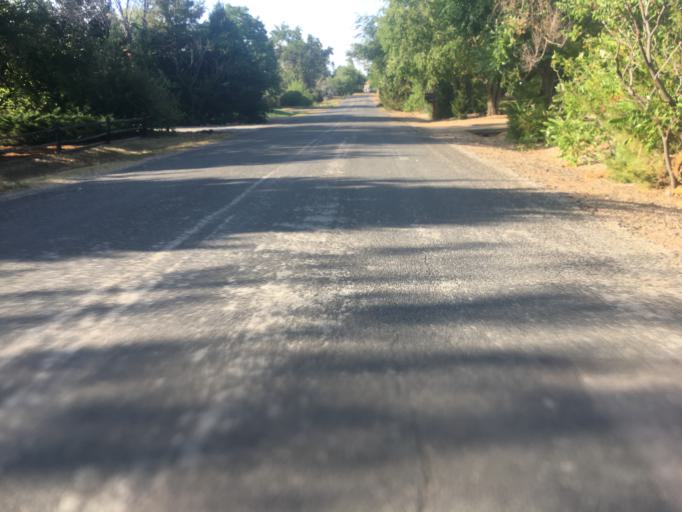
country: US
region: Colorado
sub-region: Boulder County
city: Louisville
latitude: 39.9947
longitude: -105.1257
